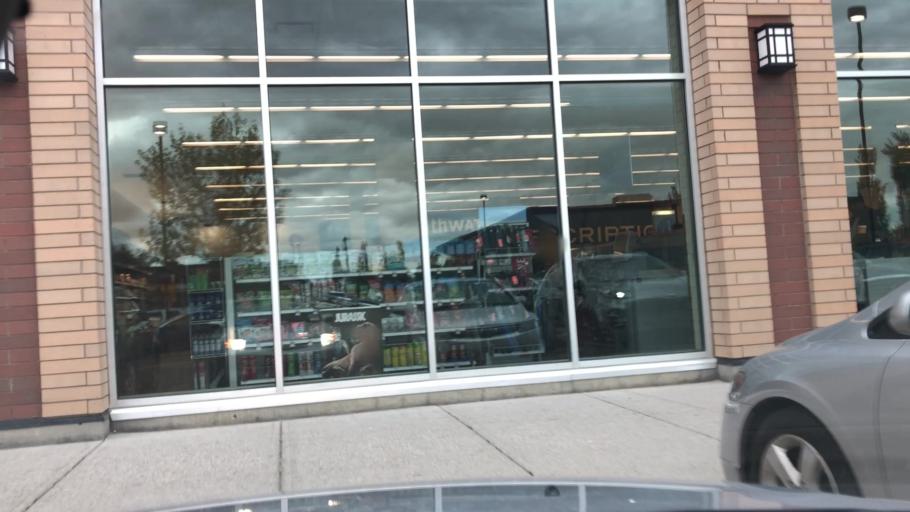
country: CA
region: Alberta
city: St. Albert
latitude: 53.6164
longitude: -113.5431
